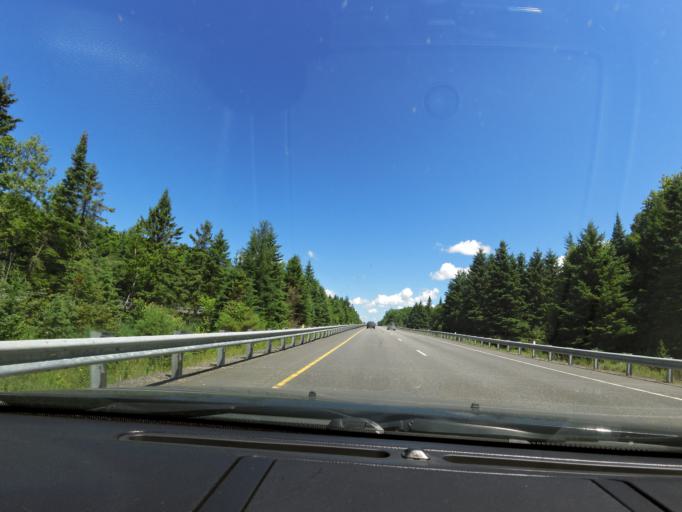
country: CA
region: Ontario
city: Bracebridge
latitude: 45.1436
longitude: -79.3110
